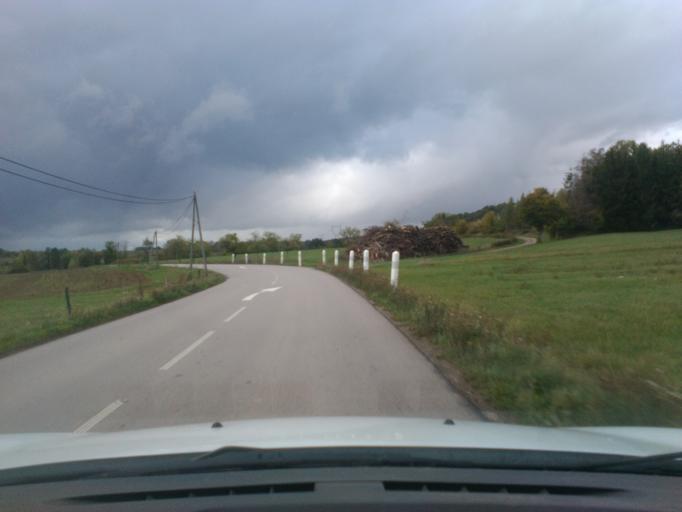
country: FR
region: Lorraine
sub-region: Departement des Vosges
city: Deyvillers
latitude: 48.2599
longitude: 6.5307
